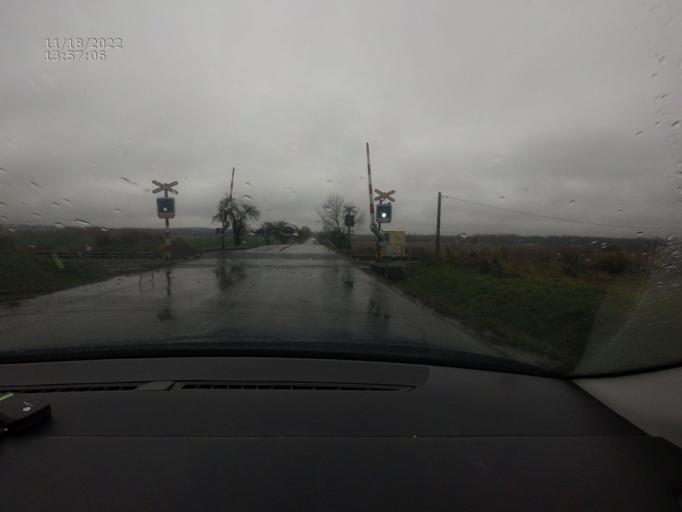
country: CZ
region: Jihocesky
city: Sedlice
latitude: 49.3693
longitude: 13.9545
